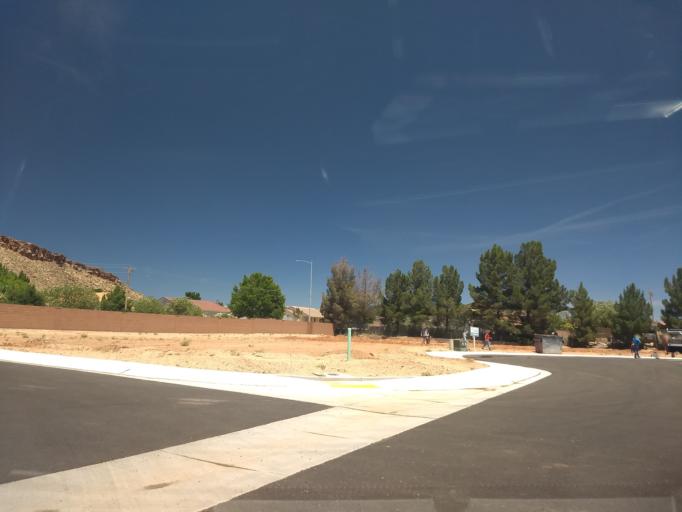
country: US
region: Utah
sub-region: Washington County
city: Saint George
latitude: 37.0663
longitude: -113.5448
